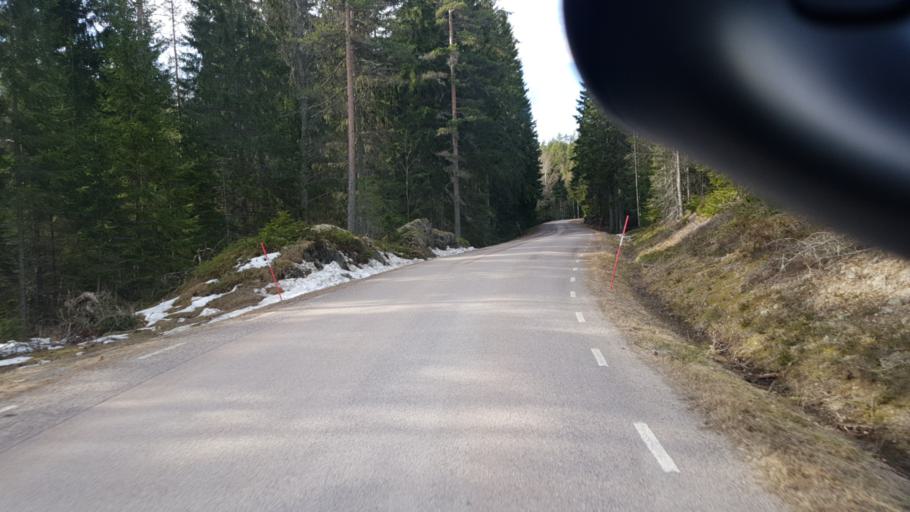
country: SE
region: Vaermland
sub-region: Arvika Kommun
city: Arvika
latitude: 59.5405
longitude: 12.5148
